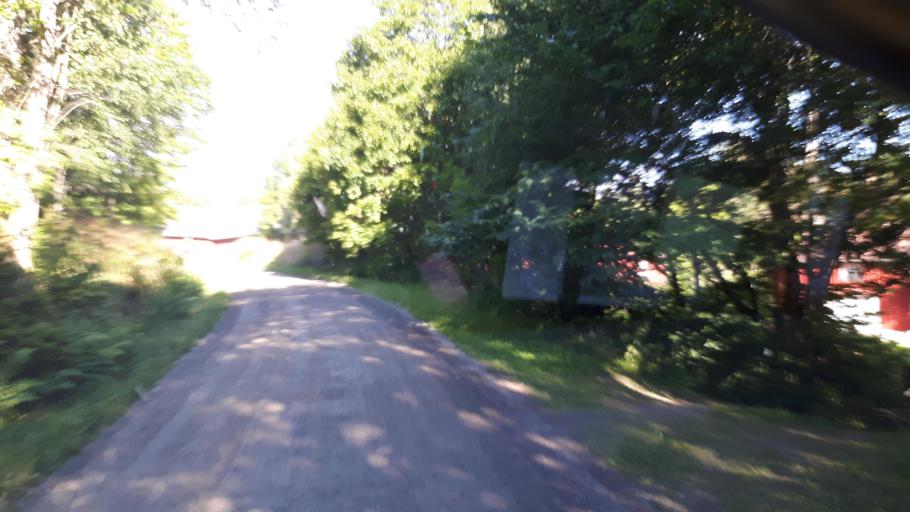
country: SE
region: OEstergoetland
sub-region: Kinda Kommun
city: Kisa
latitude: 58.0636
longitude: 15.6112
